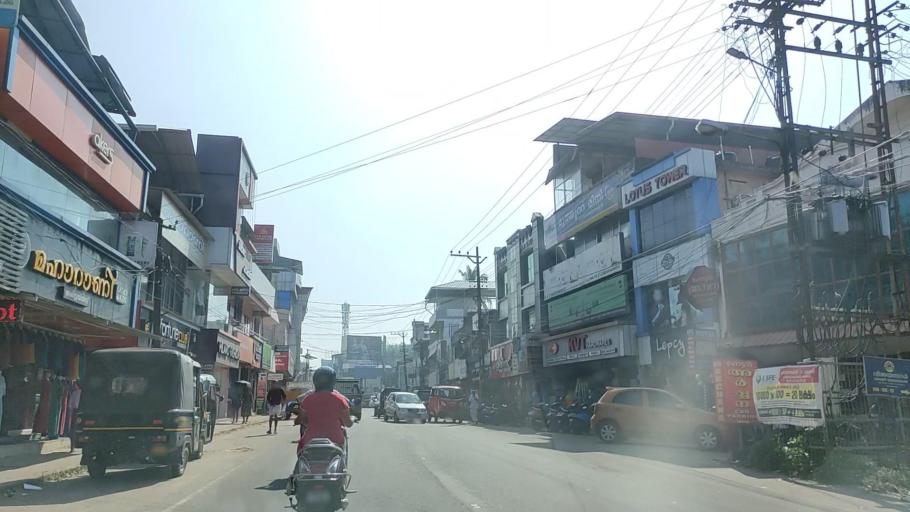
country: IN
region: Kerala
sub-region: Kollam
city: Punalur
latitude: 8.9279
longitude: 76.9127
